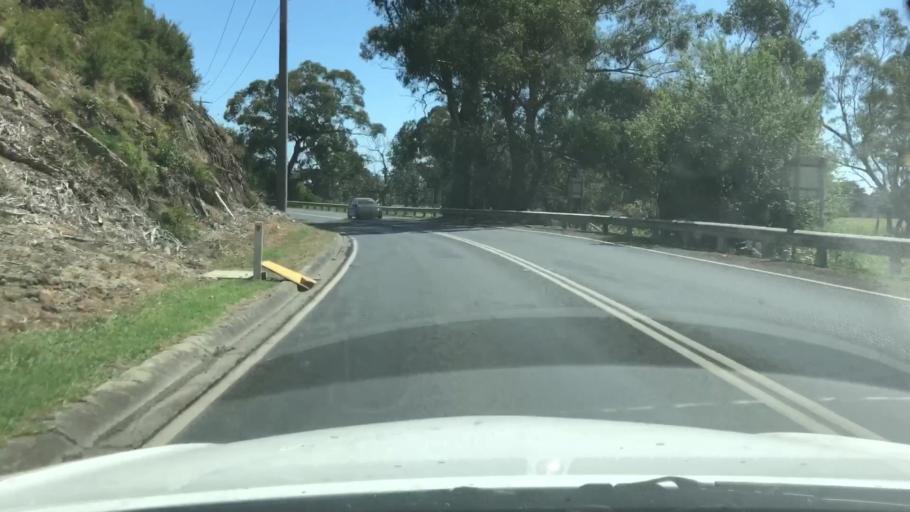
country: AU
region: Victoria
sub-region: Yarra Ranges
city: Millgrove
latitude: -37.7578
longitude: 145.6508
